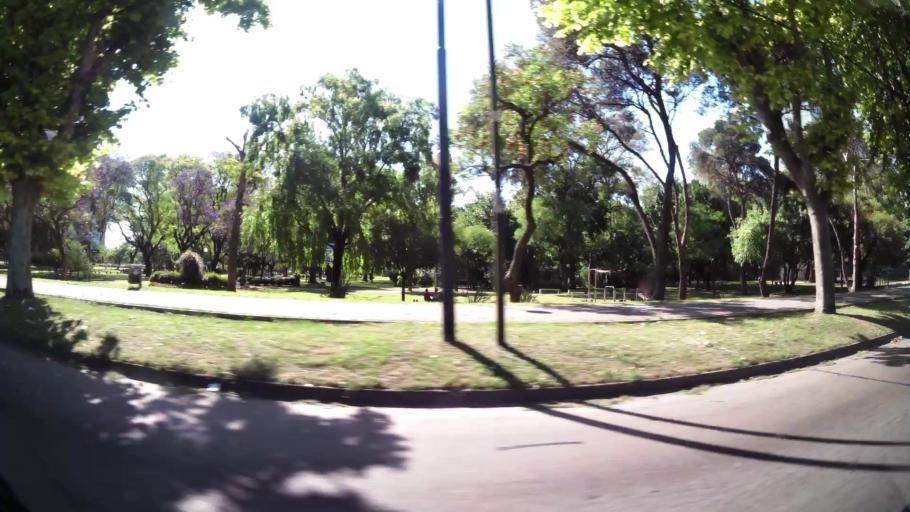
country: AR
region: Buenos Aires F.D.
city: Villa Lugano
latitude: -34.6908
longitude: -58.4625
